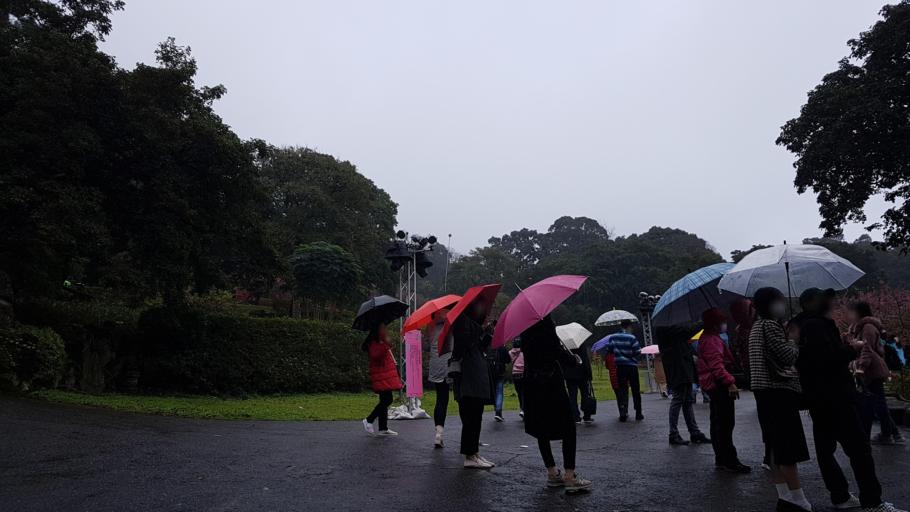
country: TW
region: Taipei
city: Taipei
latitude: 25.1856
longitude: 121.4880
